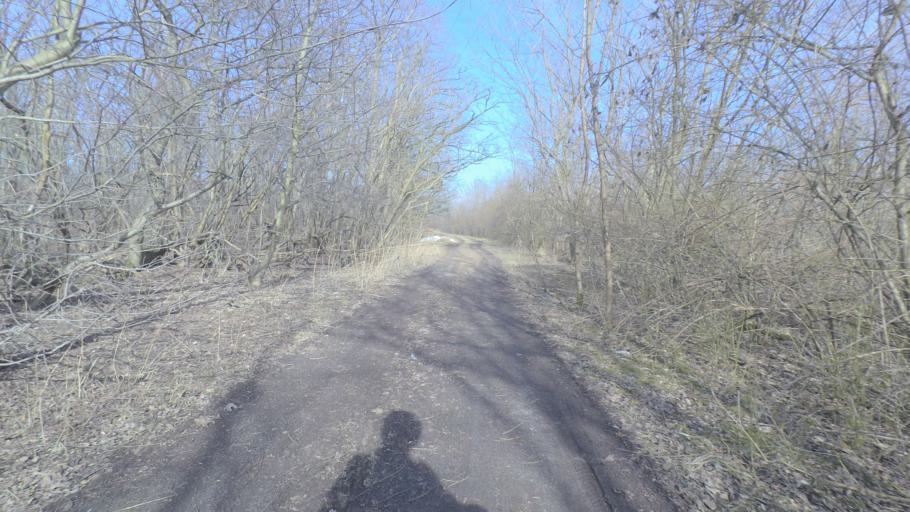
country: DE
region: Brandenburg
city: Ludwigsfelde
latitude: 52.3070
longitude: 13.2838
